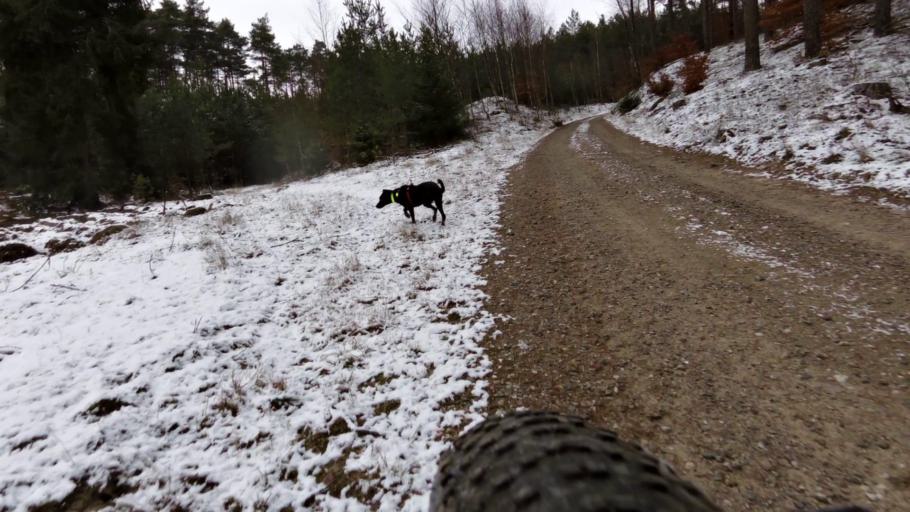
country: PL
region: West Pomeranian Voivodeship
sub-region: Powiat walecki
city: Miroslawiec
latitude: 53.3247
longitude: 16.0975
